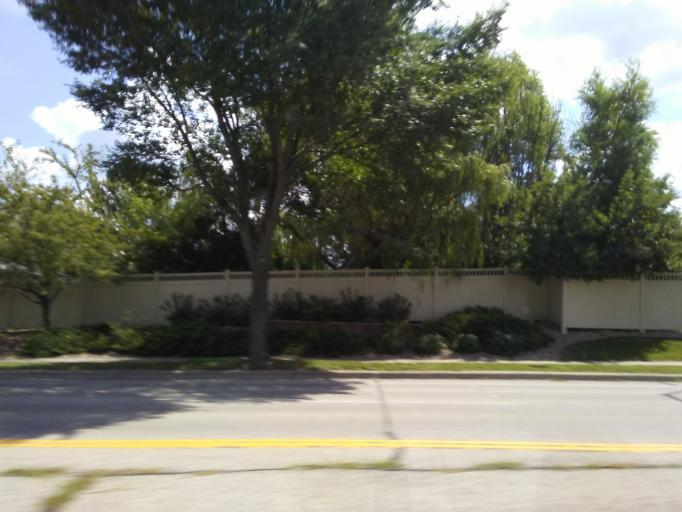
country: US
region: Wisconsin
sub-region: Dane County
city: Verona
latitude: 43.0379
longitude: -89.5183
